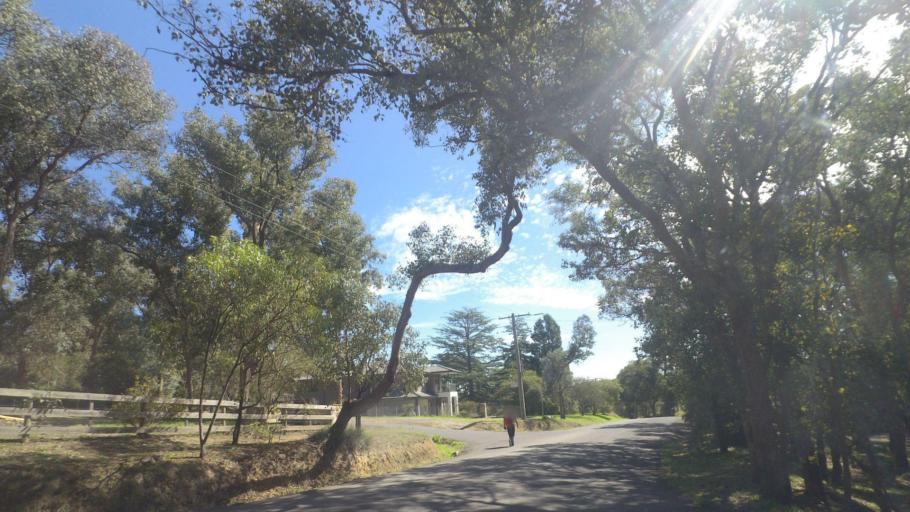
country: AU
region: Victoria
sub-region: Manningham
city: Warrandyte
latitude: -37.7407
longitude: 145.2238
